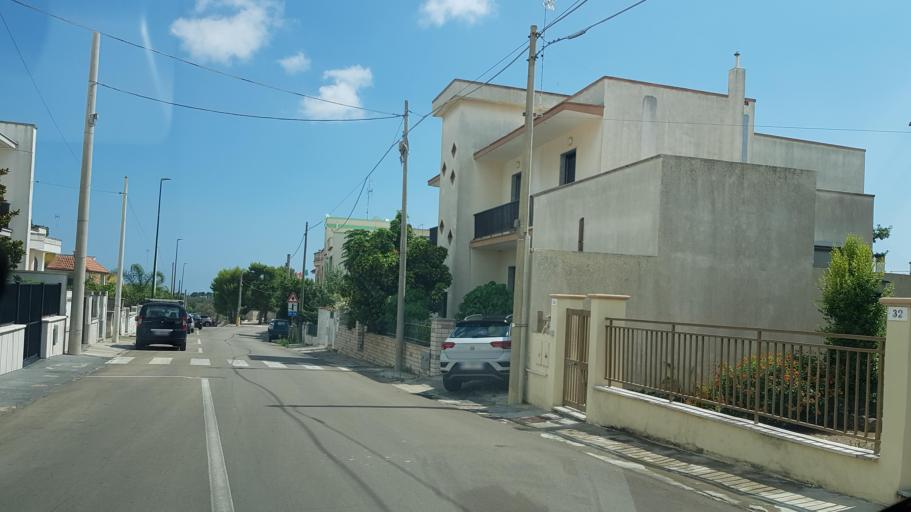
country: IT
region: Apulia
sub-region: Provincia di Lecce
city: Castrignano del Capo
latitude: 39.8307
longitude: 18.3522
